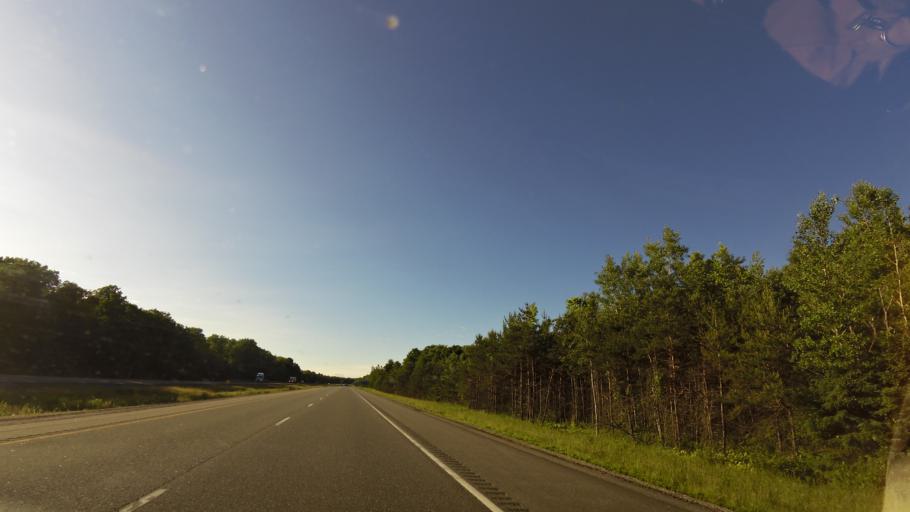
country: CA
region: Ontario
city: Barrie
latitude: 44.5321
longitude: -79.7463
